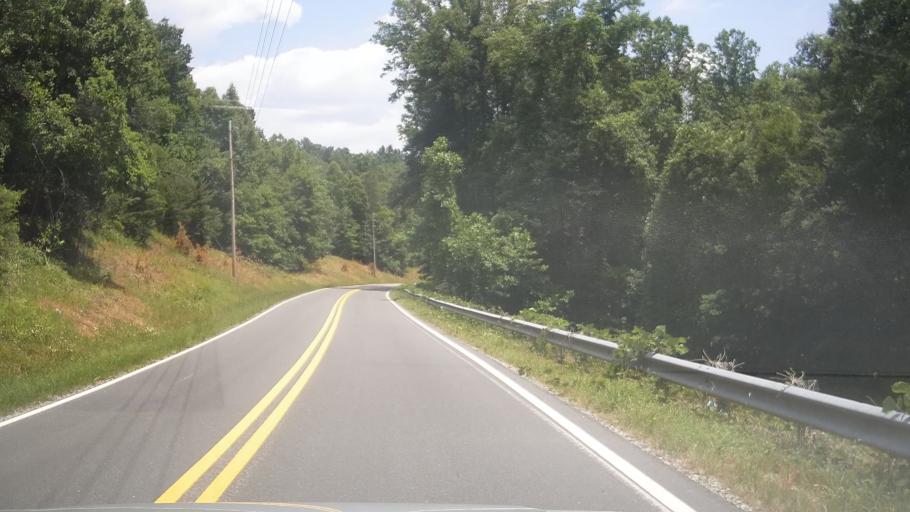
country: US
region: North Carolina
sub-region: Polk County
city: Columbus
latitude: 35.3218
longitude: -82.0897
